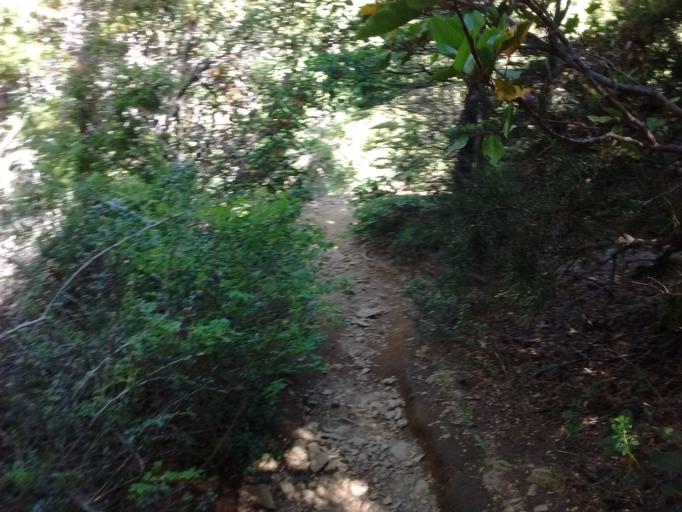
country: AR
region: Rio Negro
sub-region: Departamento de Bariloche
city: San Carlos de Bariloche
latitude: -41.0723
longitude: -71.5791
